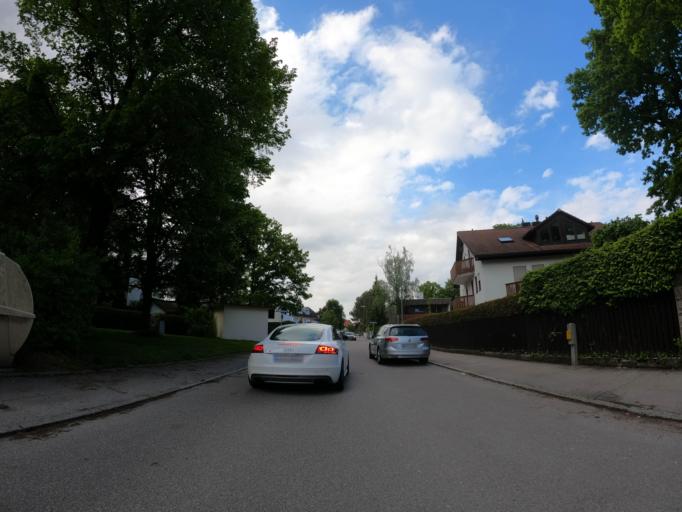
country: DE
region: Bavaria
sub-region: Upper Bavaria
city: Neubiberg
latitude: 48.0789
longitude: 11.6649
